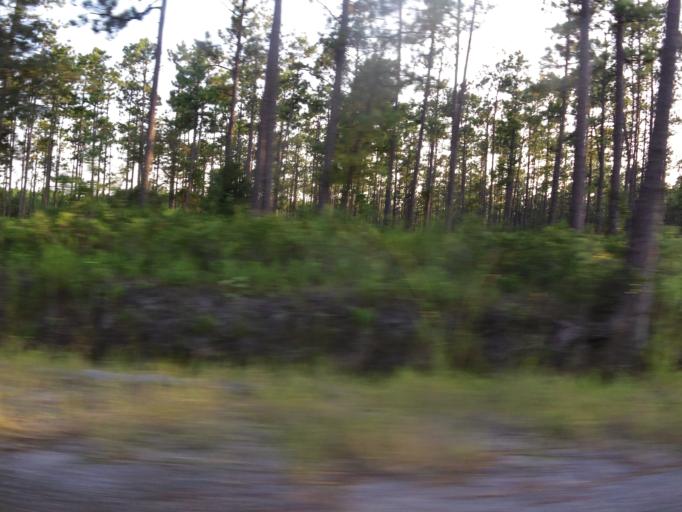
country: US
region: Florida
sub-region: Baker County
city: Macclenny
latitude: 30.3892
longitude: -82.0832
